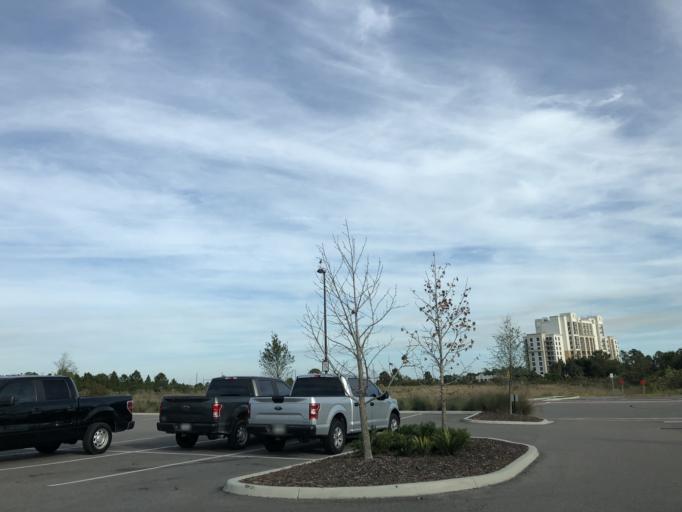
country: US
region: Florida
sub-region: Orange County
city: Tangelo Park
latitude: 28.4350
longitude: -81.4636
